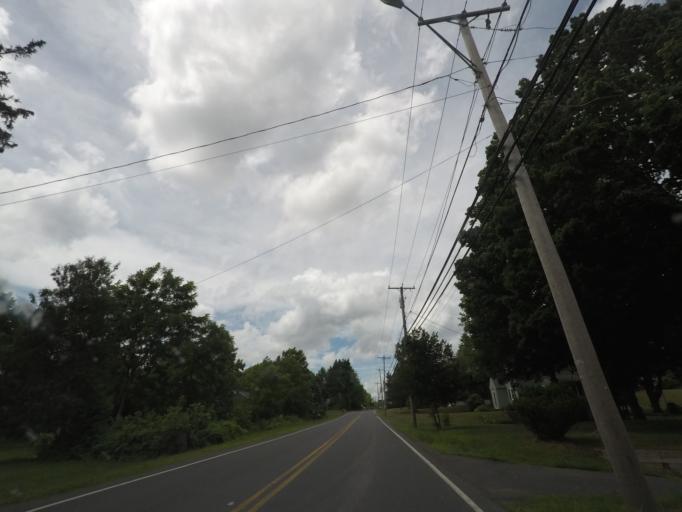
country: US
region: New York
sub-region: Rensselaer County
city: Wynantskill
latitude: 42.7083
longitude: -73.6265
